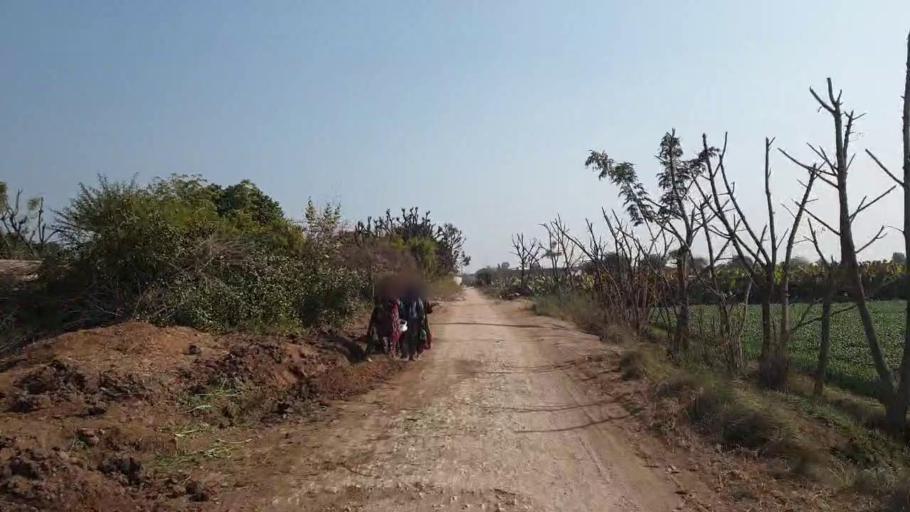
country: PK
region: Sindh
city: Hala
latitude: 25.8894
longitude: 68.4108
